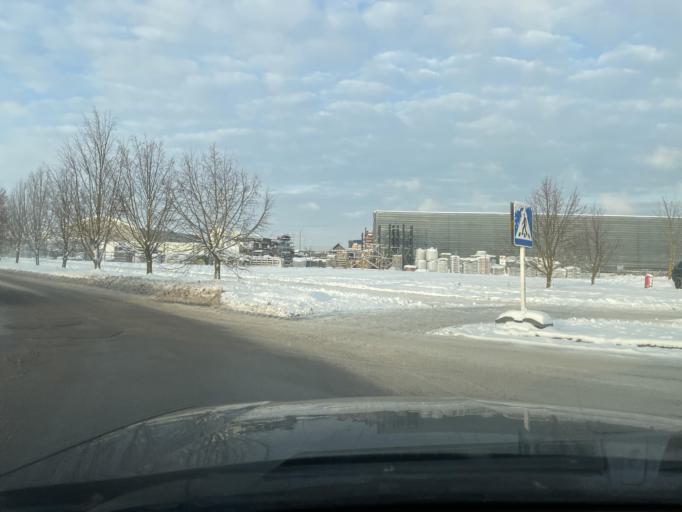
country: EE
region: Tartu
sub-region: Tartu linn
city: Tartu
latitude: 58.3555
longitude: 26.6899
